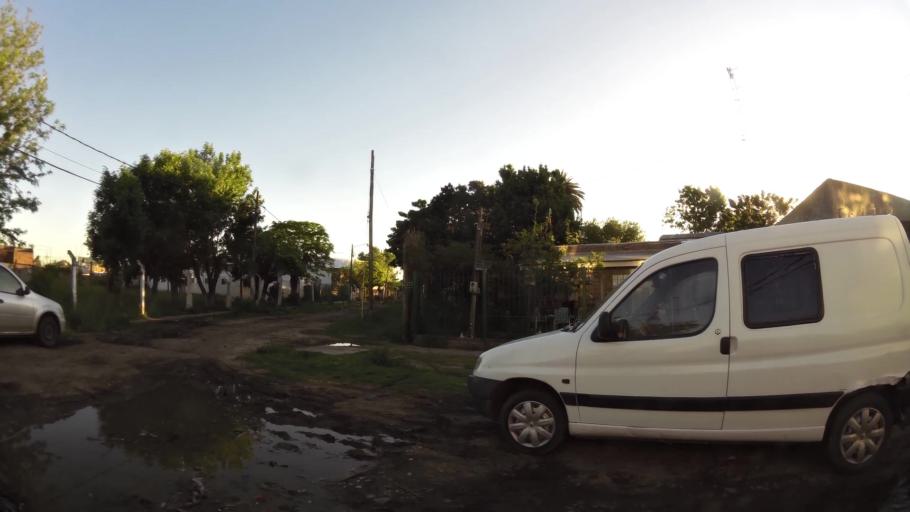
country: AR
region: Buenos Aires
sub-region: Partido de Almirante Brown
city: Adrogue
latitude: -34.7826
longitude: -58.3367
